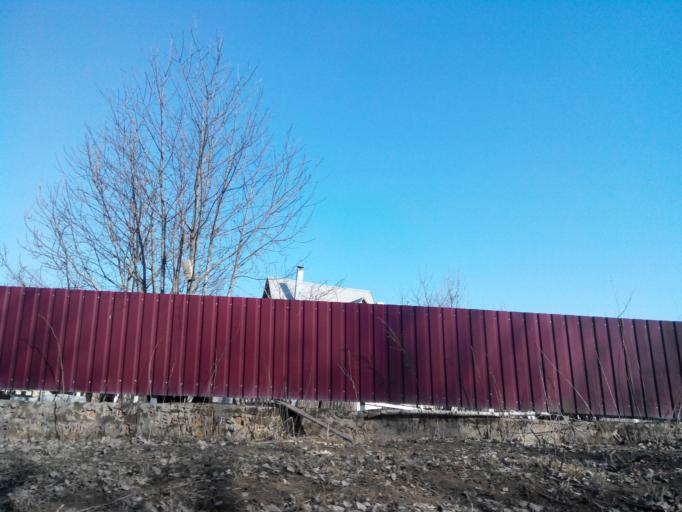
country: BY
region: Minsk
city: Zhdanovichy
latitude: 53.9216
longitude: 27.4001
